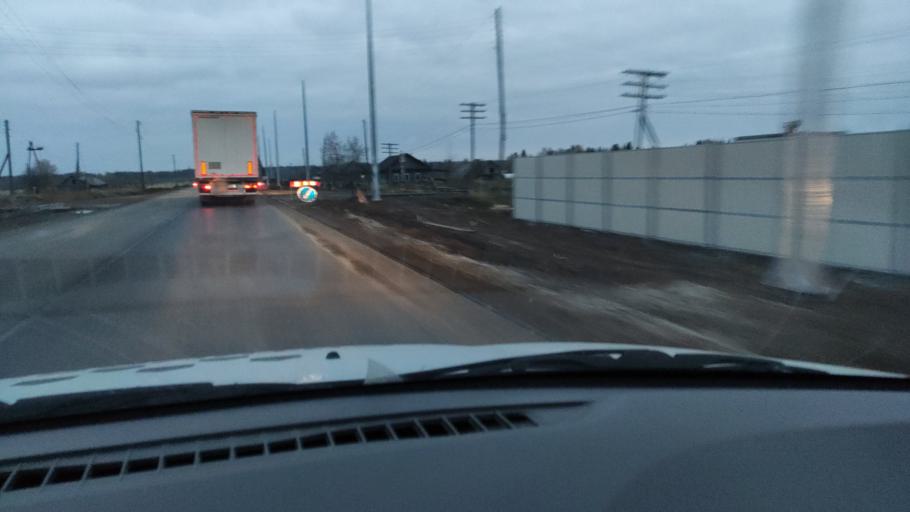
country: RU
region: Kirov
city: Kostino
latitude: 58.8316
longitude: 53.3073
